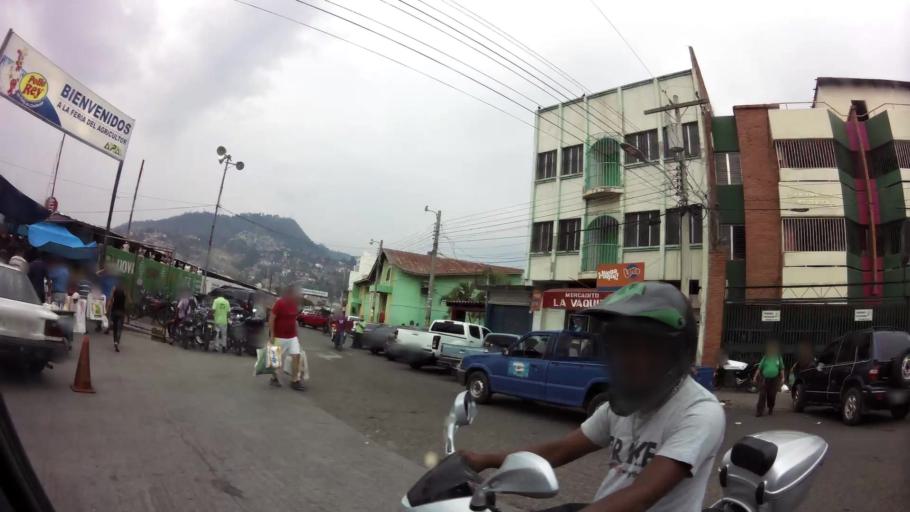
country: HN
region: Francisco Morazan
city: Tegucigalpa
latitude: 14.0996
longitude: -87.2032
